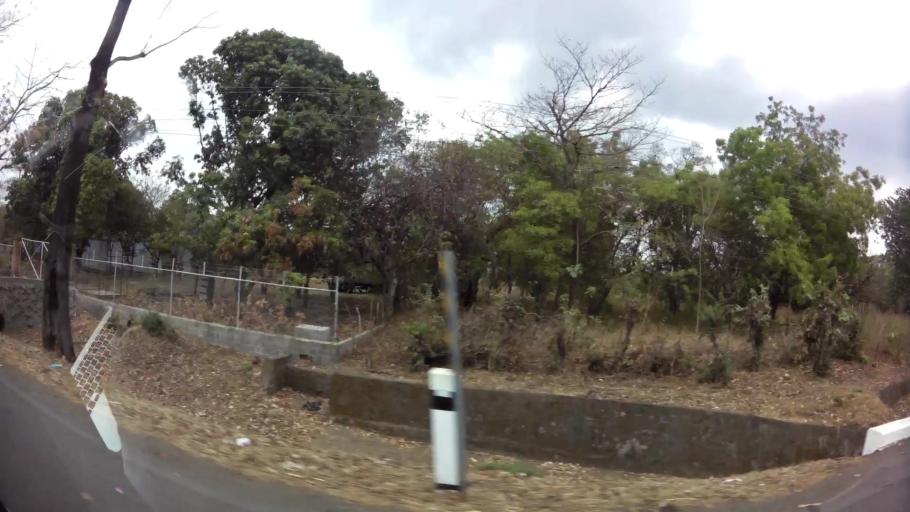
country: NI
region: Leon
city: Telica
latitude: 12.4891
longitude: -86.8609
